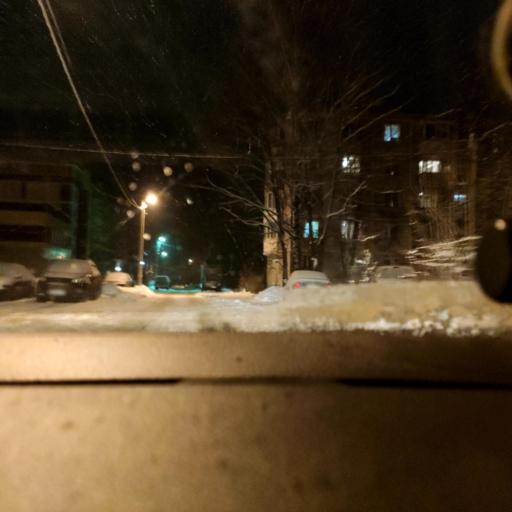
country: RU
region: Moskovskaya
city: Iksha
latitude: 56.1793
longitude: 37.4955
